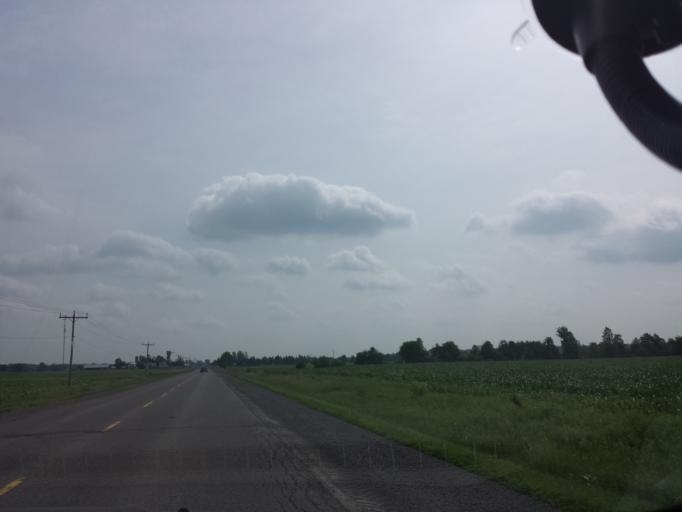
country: CA
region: Ontario
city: Bourget
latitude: 45.4131
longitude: -75.2358
